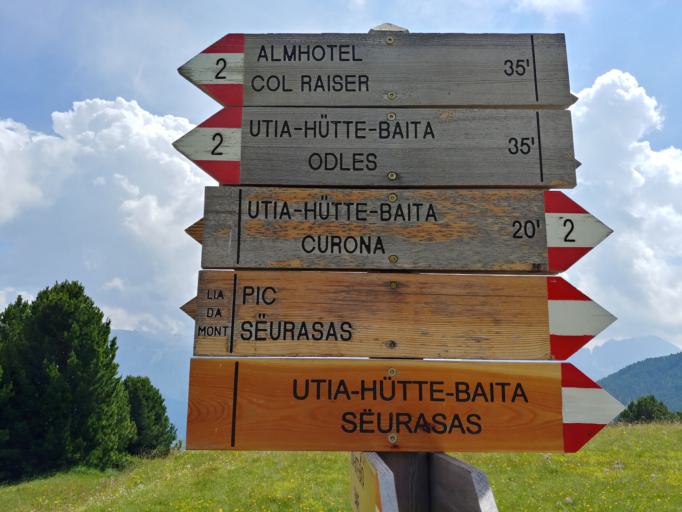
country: IT
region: Trentino-Alto Adige
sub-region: Bolzano
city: Santa Cristina Valgardena
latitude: 46.5918
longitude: 11.7318
